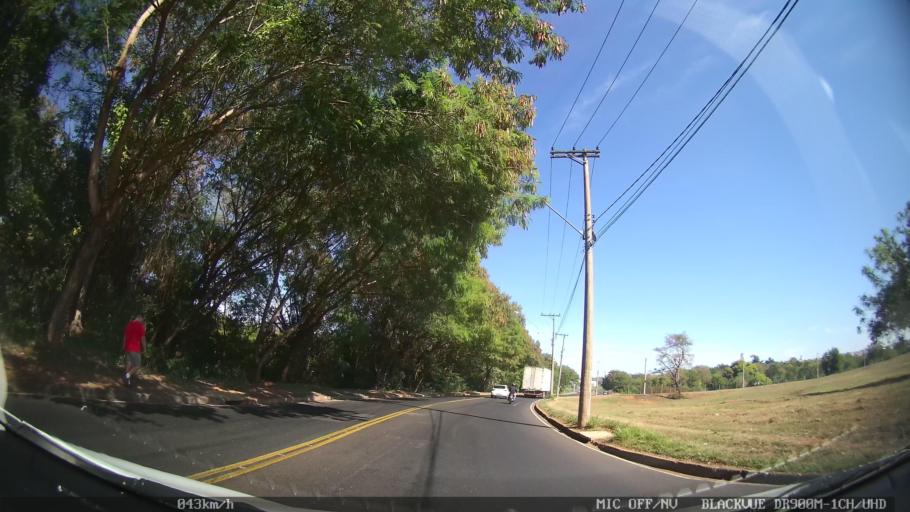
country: BR
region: Sao Paulo
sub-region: Sao Jose Do Rio Preto
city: Sao Jose do Rio Preto
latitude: -20.8048
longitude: -49.4222
